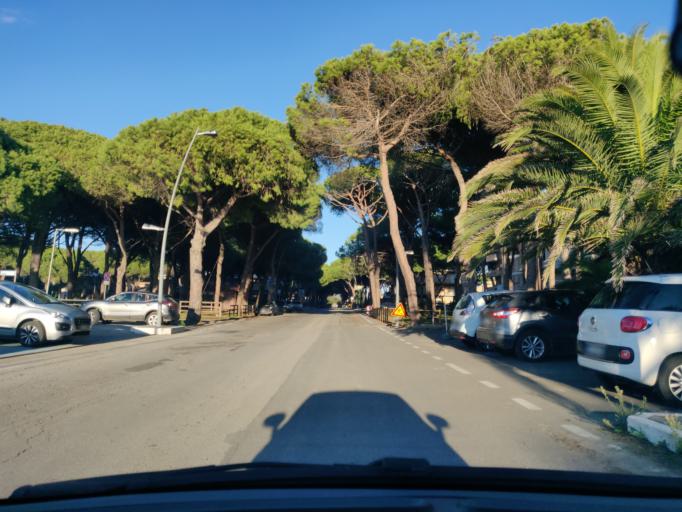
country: IT
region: Latium
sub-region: Provincia di Viterbo
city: Tarquinia
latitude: 42.2180
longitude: 11.7097
